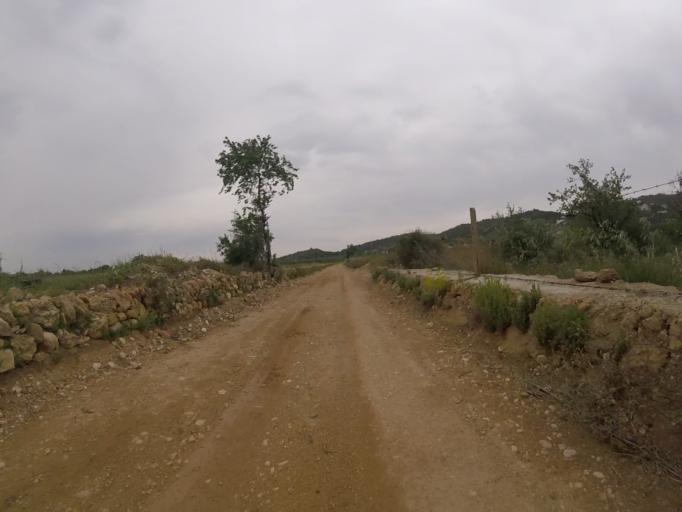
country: ES
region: Valencia
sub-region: Provincia de Castello
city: Alcoceber
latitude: 40.2434
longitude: 0.2614
